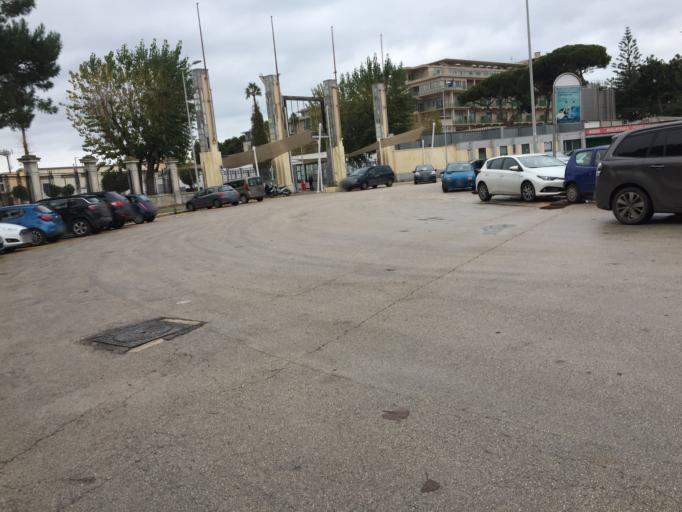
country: IT
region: Apulia
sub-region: Provincia di Bari
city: Bari
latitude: 41.1346
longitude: 16.8440
